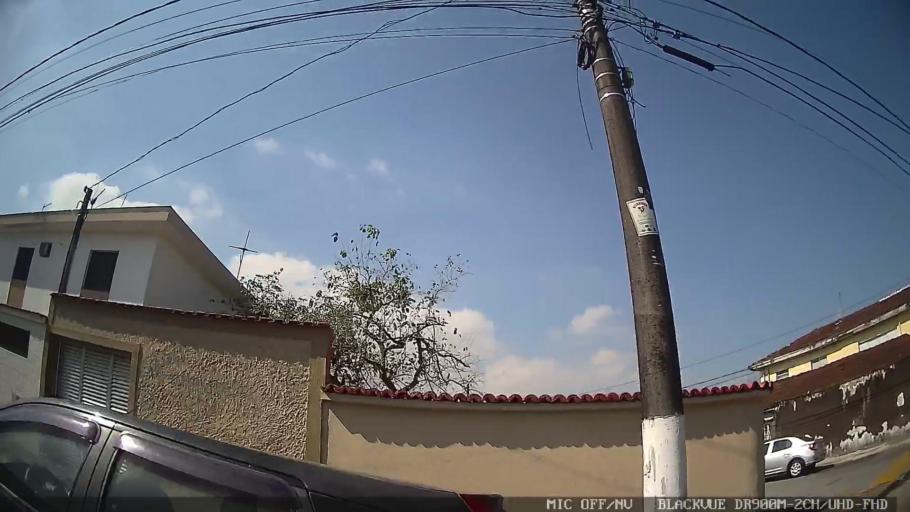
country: BR
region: Sao Paulo
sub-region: Santos
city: Santos
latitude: -23.9391
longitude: -46.3041
